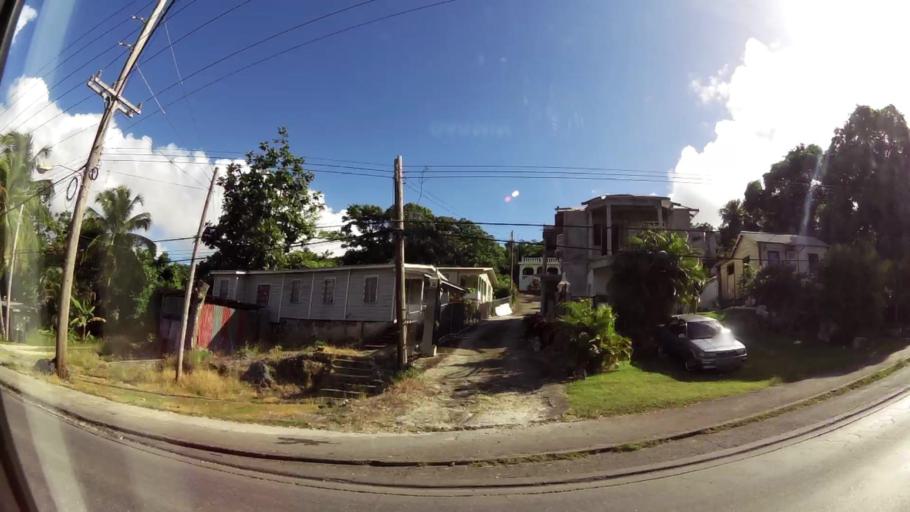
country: BB
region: Saint James
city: Holetown
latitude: 13.2140
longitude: -59.6188
